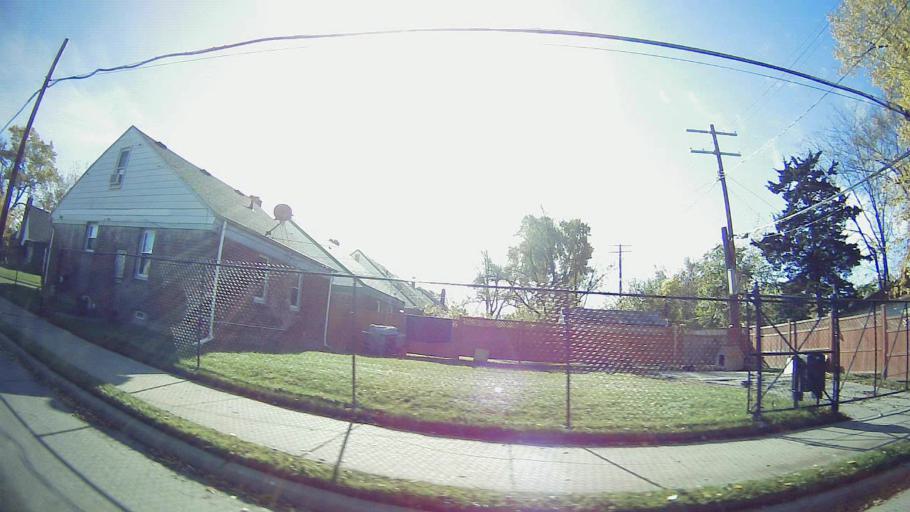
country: US
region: Michigan
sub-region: Wayne County
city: Highland Park
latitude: 42.3886
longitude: -83.1520
